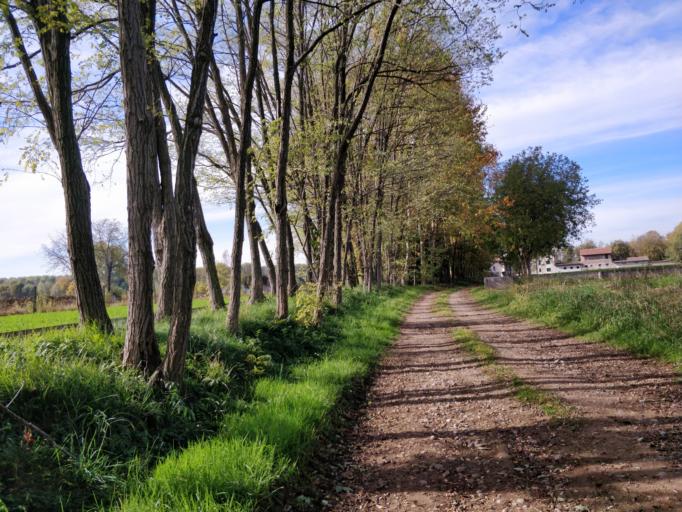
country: IT
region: Friuli Venezia Giulia
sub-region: Provincia di Udine
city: Bertiolo
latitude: 45.9405
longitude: 13.0291
